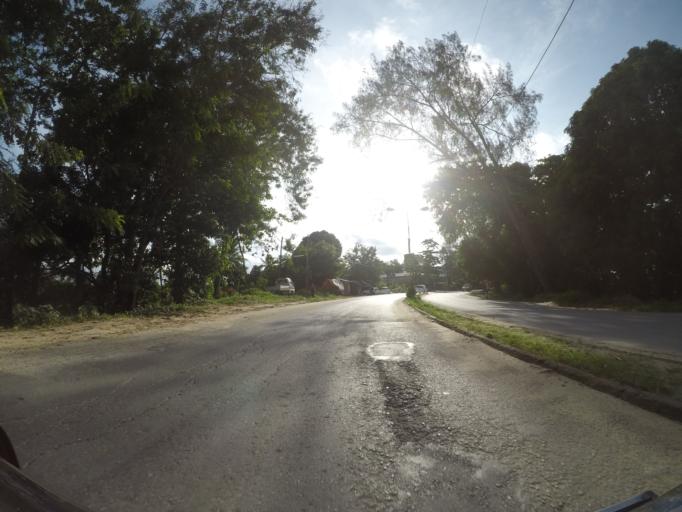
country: TZ
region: Pemba South
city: Chake Chake
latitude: -5.2399
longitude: 39.7733
